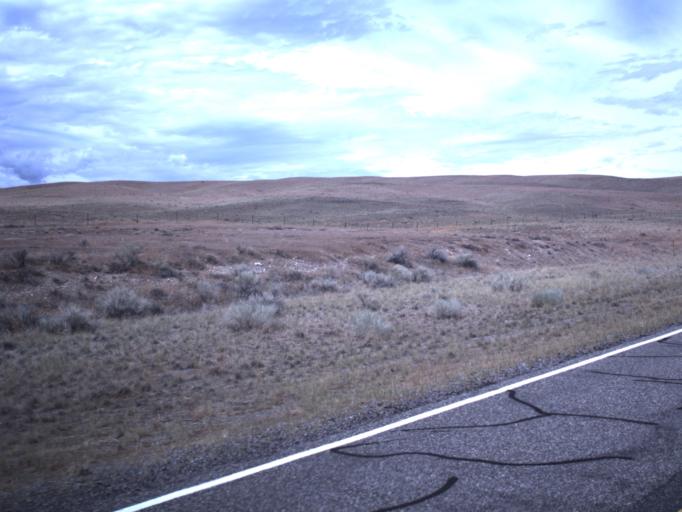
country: US
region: Utah
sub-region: Sevier County
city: Monroe
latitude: 38.6302
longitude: -112.1670
